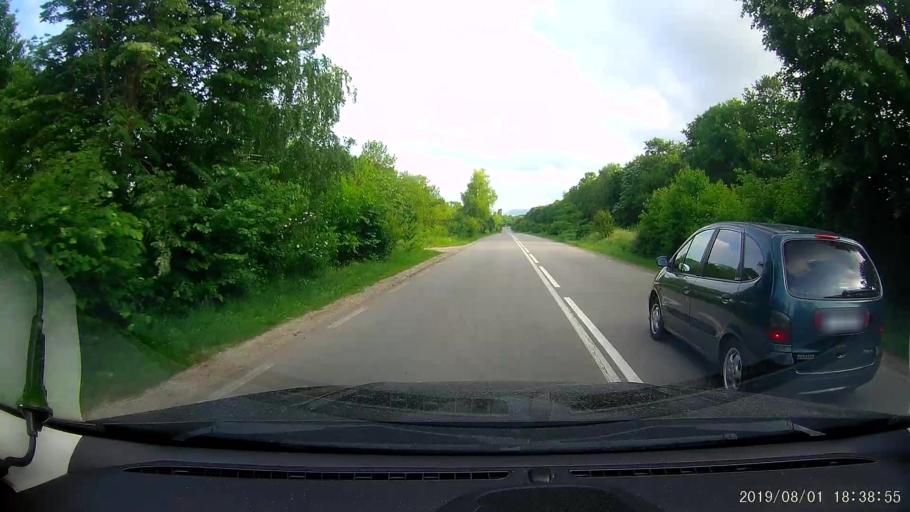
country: BG
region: Shumen
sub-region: Obshtina Khitrino
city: Gara Khitrino
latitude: 43.3958
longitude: 26.9172
